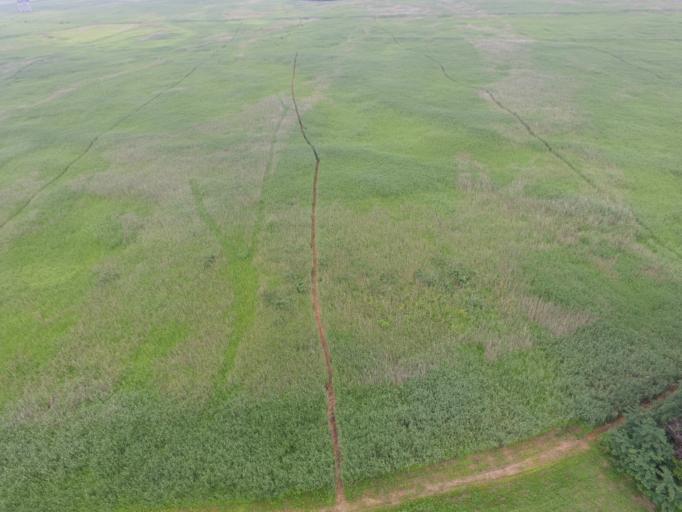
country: JP
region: Tochigi
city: Fujioka
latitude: 36.2658
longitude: 139.6799
